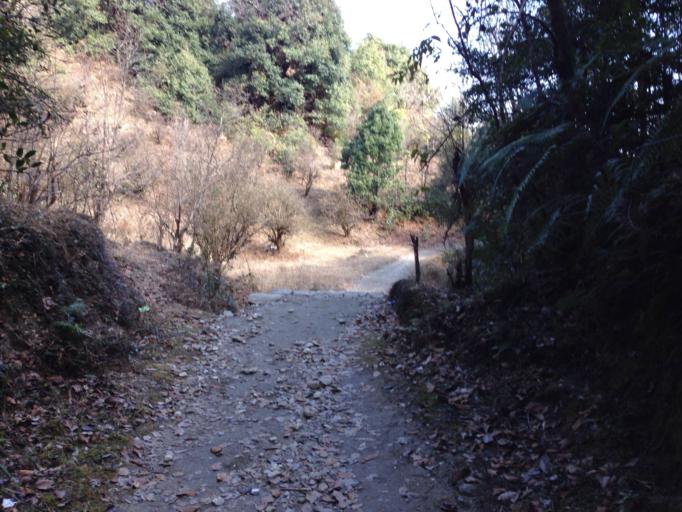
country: NP
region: Central Region
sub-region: Bagmati Zone
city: Nagarkot
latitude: 27.8134
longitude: 85.4422
